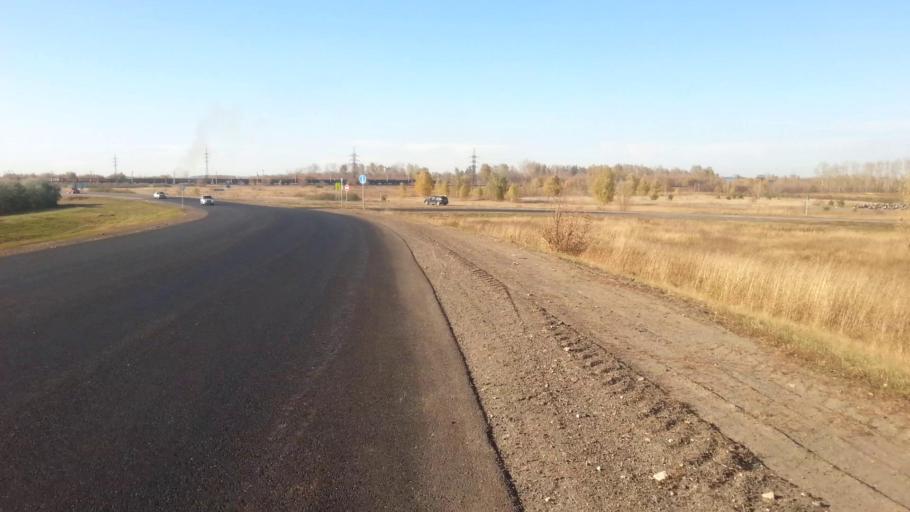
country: RU
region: Altai Krai
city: Novoaltaysk
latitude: 53.3719
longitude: 83.9537
